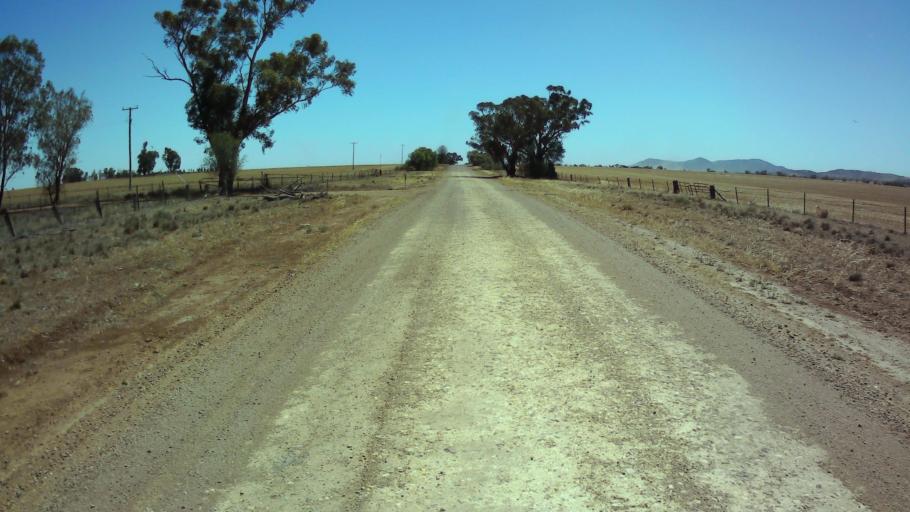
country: AU
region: New South Wales
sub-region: Forbes
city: Forbes
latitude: -33.6958
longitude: 147.7076
